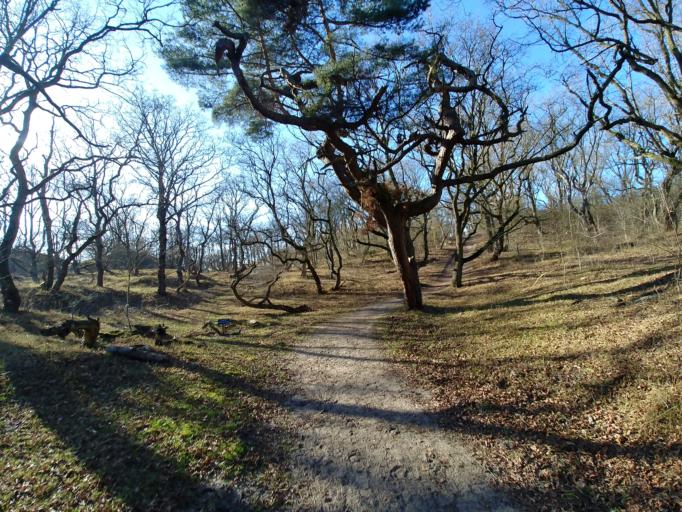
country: NL
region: South Holland
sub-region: Gemeente Den Haag
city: Scheveningen
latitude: 52.1265
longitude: 4.3254
